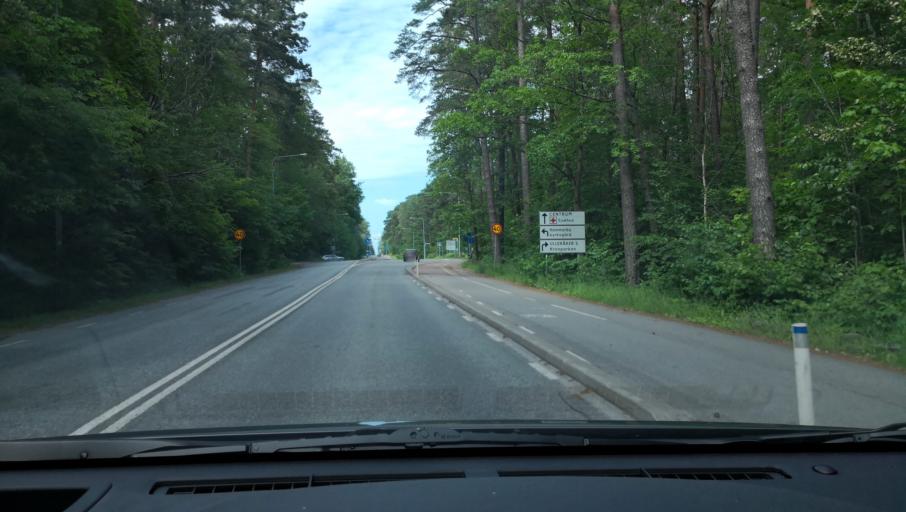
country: SE
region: Uppsala
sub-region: Uppsala Kommun
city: Uppsala
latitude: 59.8267
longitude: 17.6447
